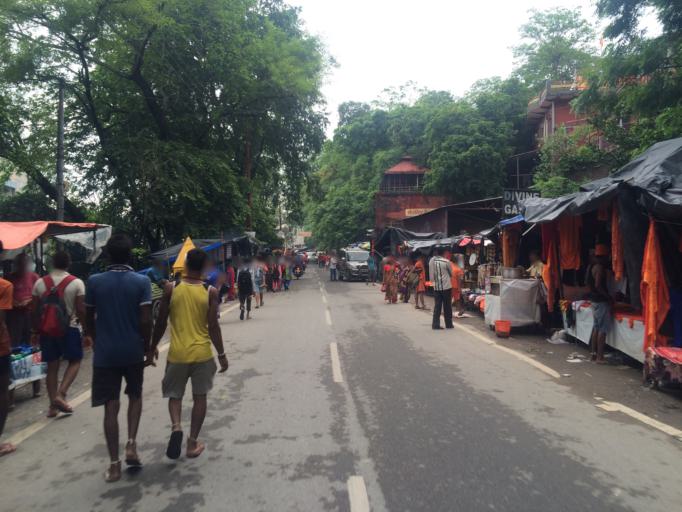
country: IN
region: Uttarakhand
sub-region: Dehradun
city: Rishikesh
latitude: 30.1192
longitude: 78.3060
